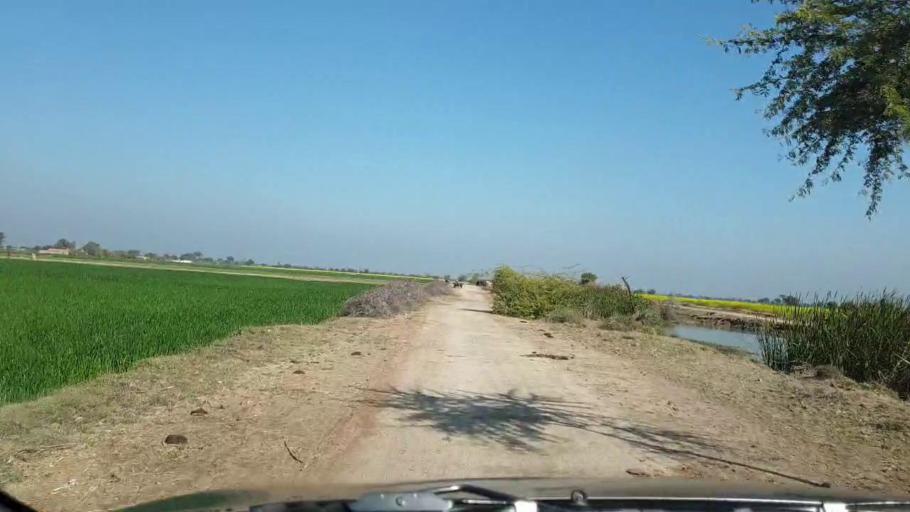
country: PK
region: Sindh
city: Sinjhoro
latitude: 25.9649
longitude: 68.7519
